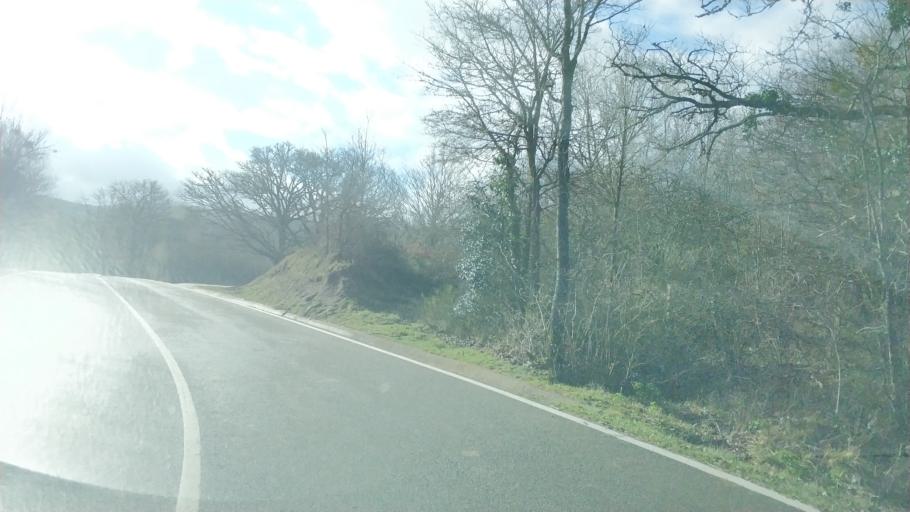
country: ES
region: Cantabria
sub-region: Provincia de Cantabria
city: Reinosa
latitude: 42.9624
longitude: -4.0611
